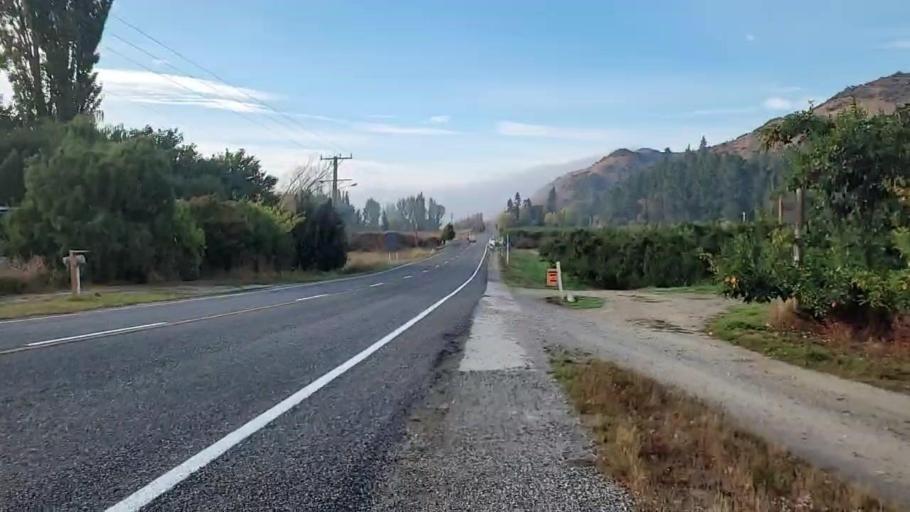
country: NZ
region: Southland
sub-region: Gore District
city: Gore
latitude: -45.6417
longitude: 169.3737
